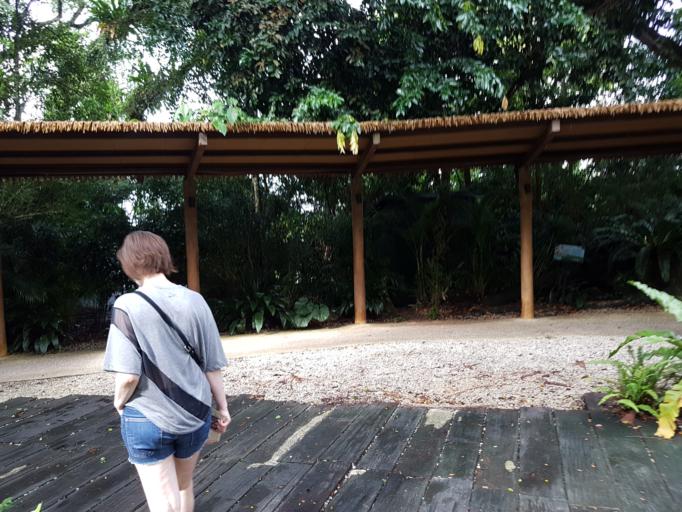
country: MY
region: Johor
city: Johor Bahru
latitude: 1.4046
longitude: 103.7918
